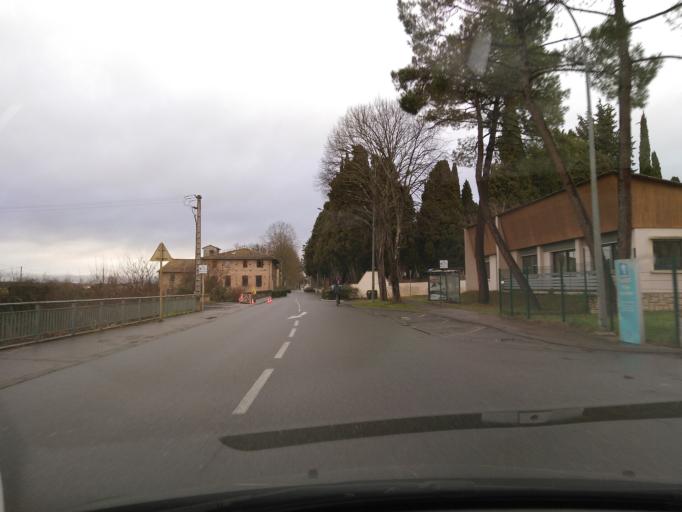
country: FR
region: Midi-Pyrenees
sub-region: Departement de la Haute-Garonne
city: Montesquieu-Volvestre
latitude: 43.2108
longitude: 1.2283
